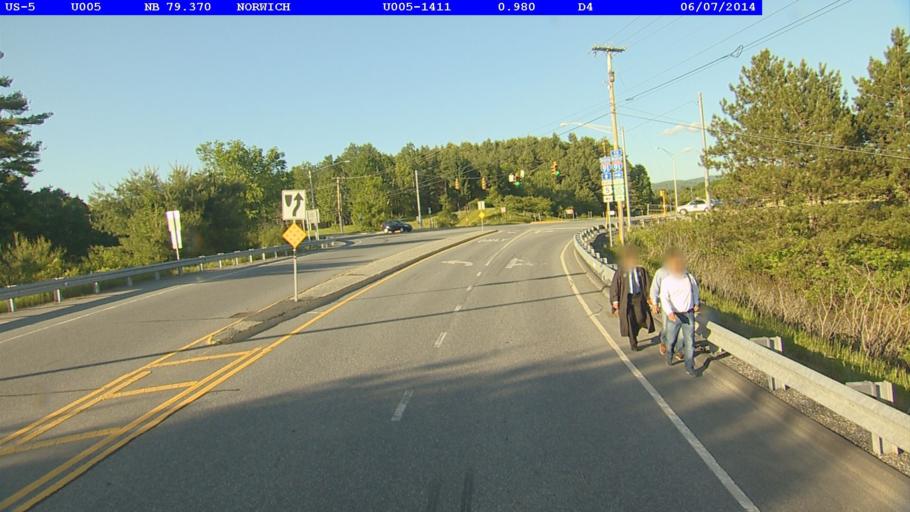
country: US
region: New Hampshire
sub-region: Grafton County
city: Hanover
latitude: 43.7077
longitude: -72.3079
